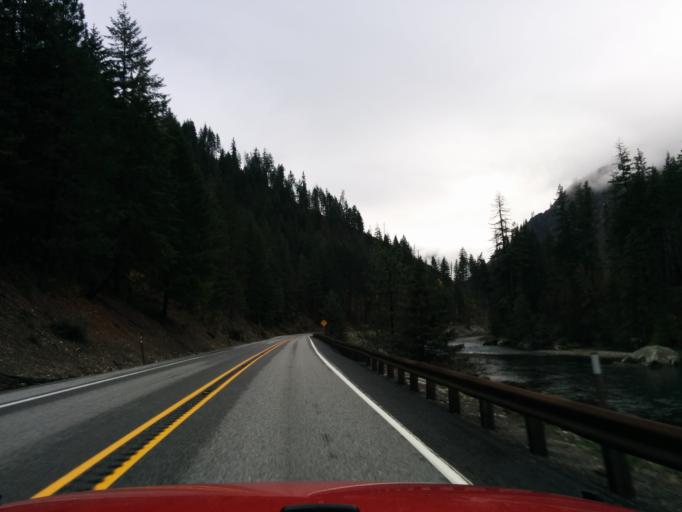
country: US
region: Washington
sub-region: Chelan County
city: Leavenworth
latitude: 47.6613
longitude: -120.7306
